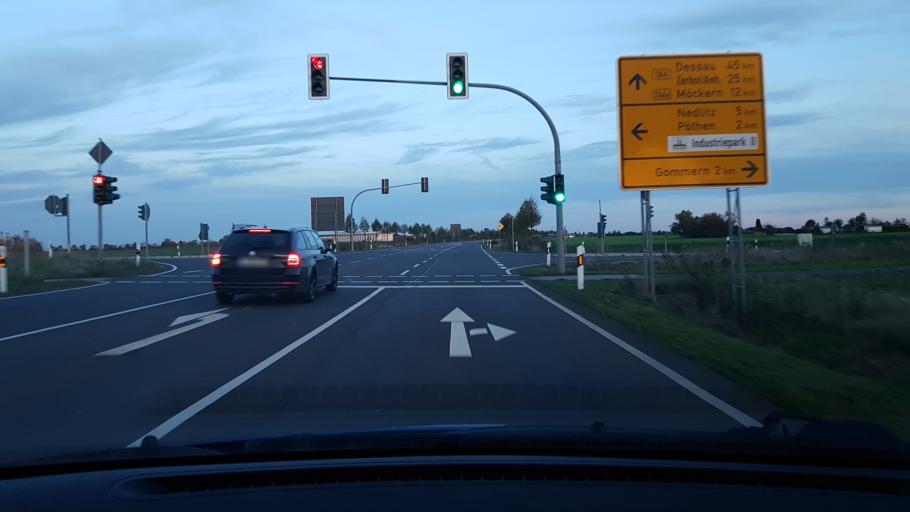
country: DE
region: Saxony-Anhalt
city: Gommern
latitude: 52.0848
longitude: 11.8296
